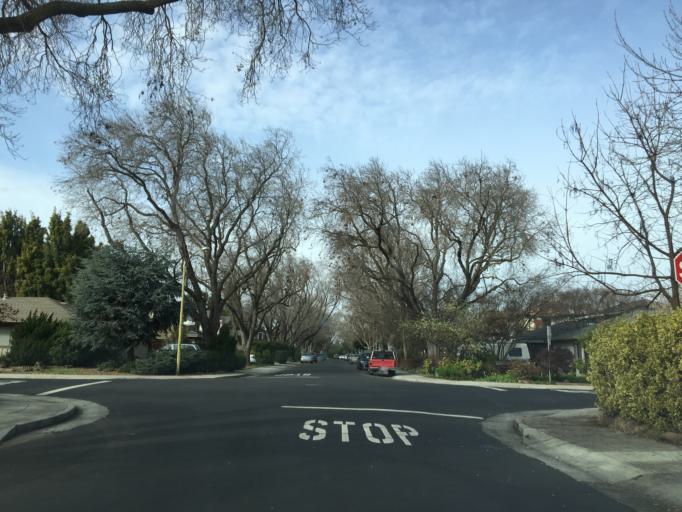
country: US
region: California
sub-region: Santa Clara County
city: Palo Alto
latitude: 37.4232
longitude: -122.1247
